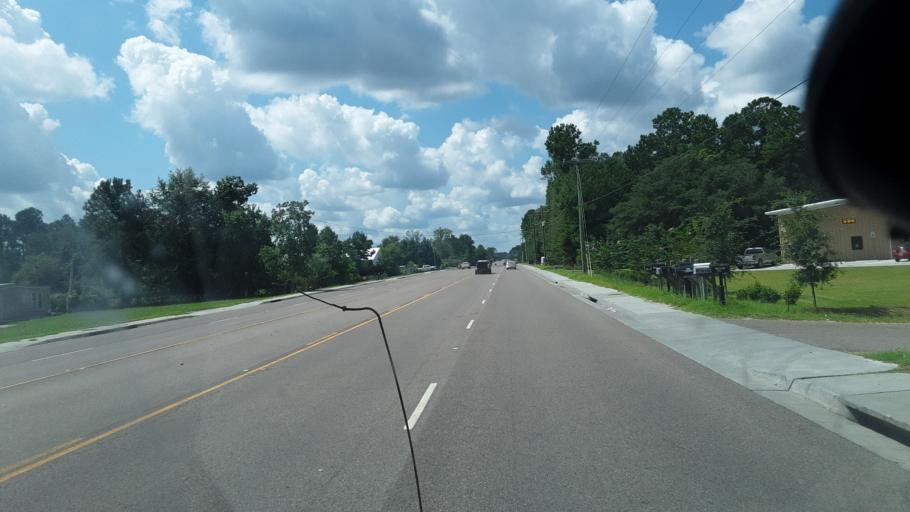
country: US
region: South Carolina
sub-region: Berkeley County
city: Moncks Corner
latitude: 33.1742
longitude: -80.0371
